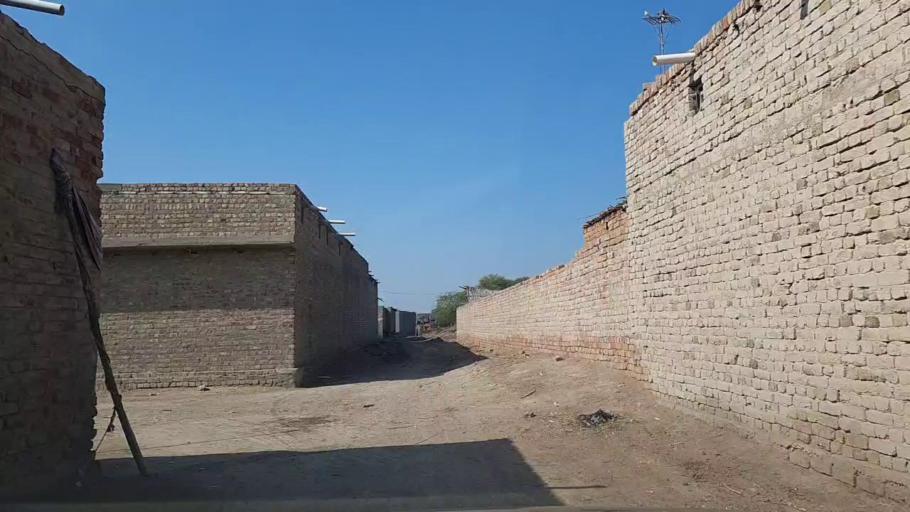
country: PK
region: Sindh
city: Nawabshah
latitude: 26.2905
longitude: 68.3779
